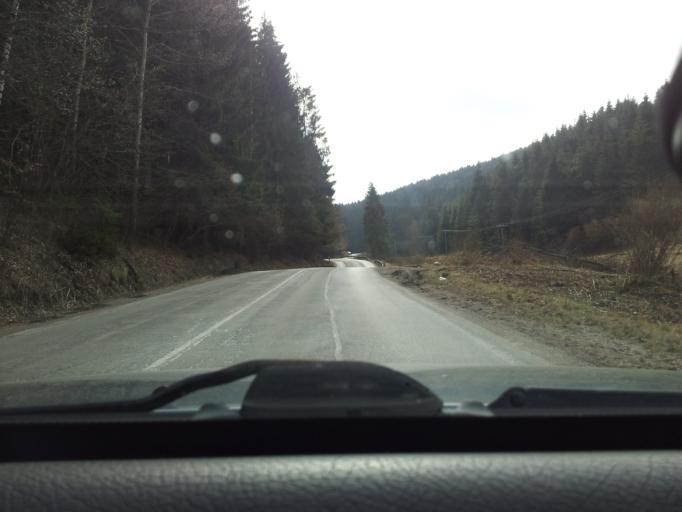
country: SK
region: Banskobystricky
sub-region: Okres Ziar nad Hronom
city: Kremnica
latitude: 48.7610
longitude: 18.9033
